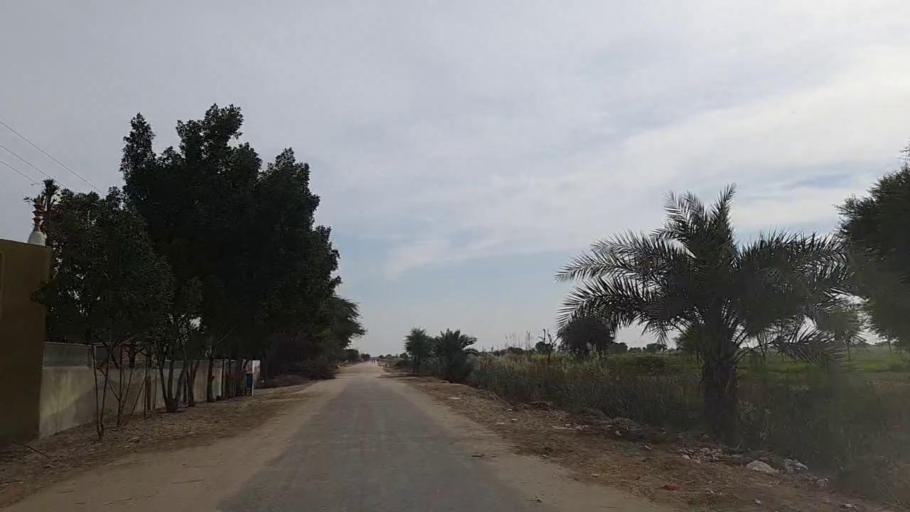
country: PK
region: Sindh
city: Daur
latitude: 26.4155
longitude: 68.4890
